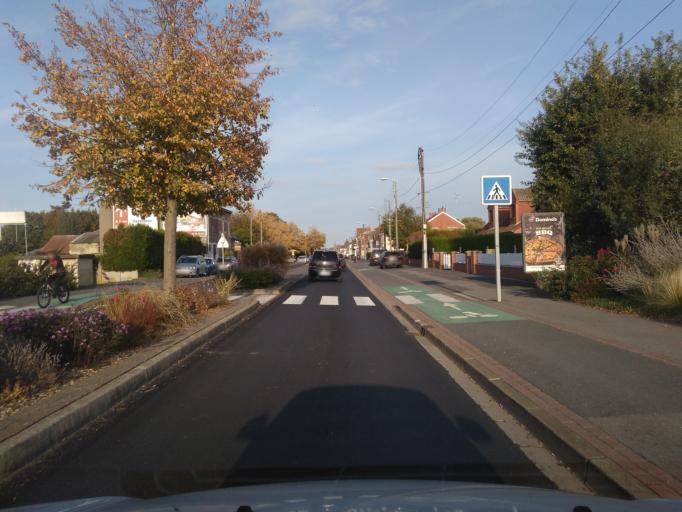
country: FR
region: Nord-Pas-de-Calais
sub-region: Departement du Nord
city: Onnaing
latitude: 50.3806
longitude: 3.5829
